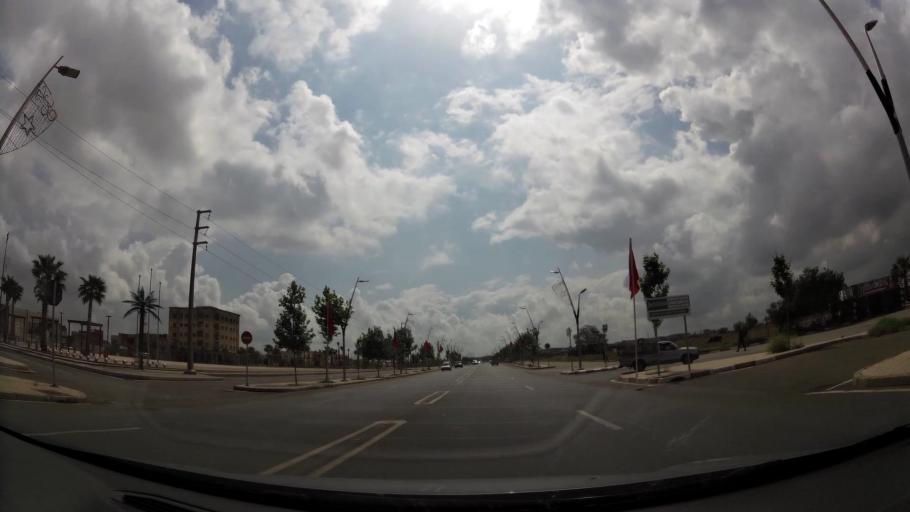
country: MA
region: Rabat-Sale-Zemmour-Zaer
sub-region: Khemisset
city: Tiflet
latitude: 33.8947
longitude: -6.3396
